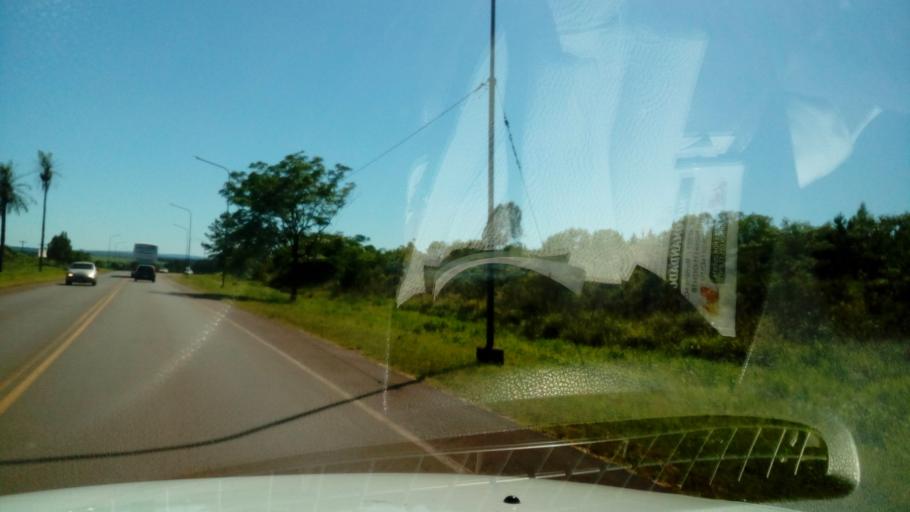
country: AR
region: Misiones
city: Santa Ana
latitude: -27.4165
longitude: -55.5288
